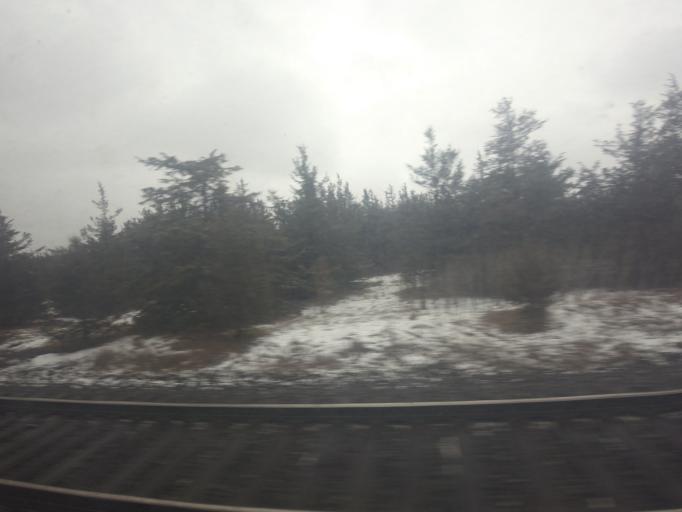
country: CA
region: Ontario
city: Belleville
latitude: 44.2055
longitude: -77.2281
